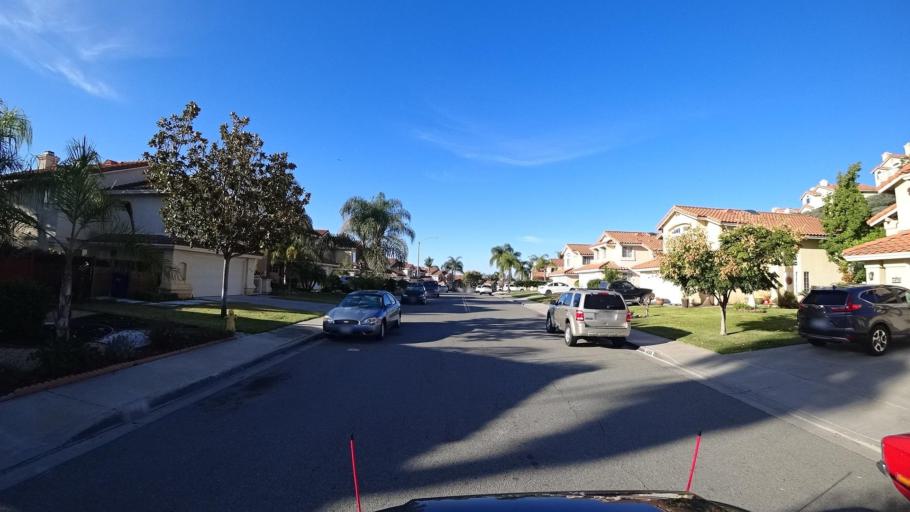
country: US
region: California
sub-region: San Diego County
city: La Presa
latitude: 32.7127
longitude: -116.9853
